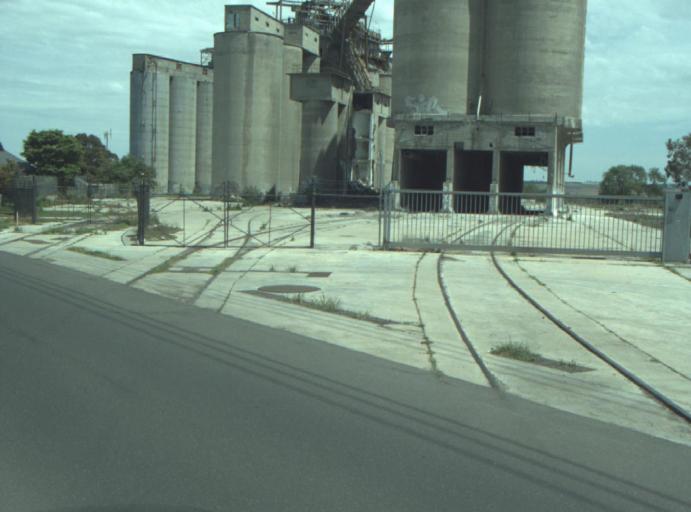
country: AU
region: Victoria
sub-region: Greater Geelong
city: Hamlyn Heights
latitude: -38.1380
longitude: 144.3185
